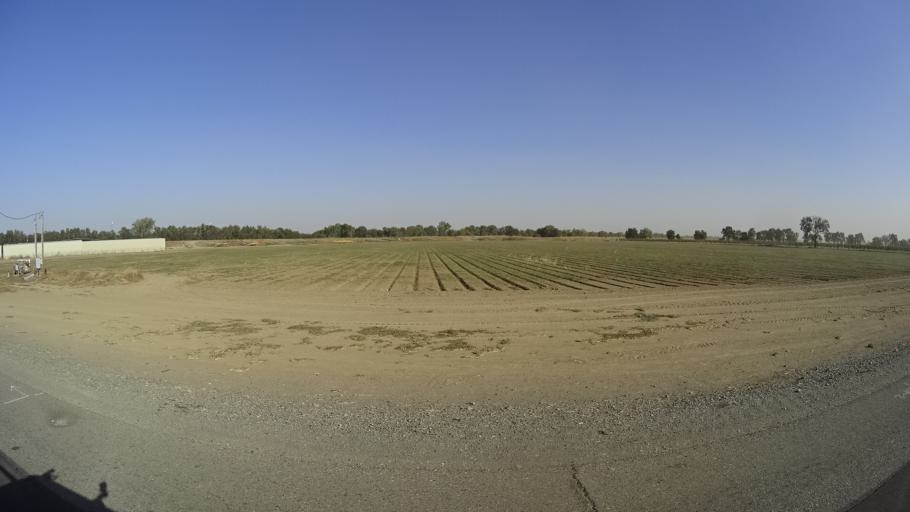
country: US
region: California
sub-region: Yolo County
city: Woodland
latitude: 38.7897
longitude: -121.7282
